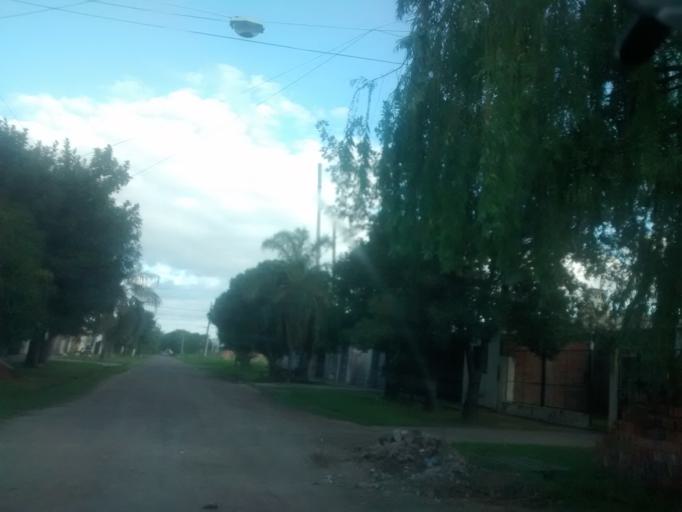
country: AR
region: Chaco
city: Fontana
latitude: -27.4538
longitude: -59.0242
